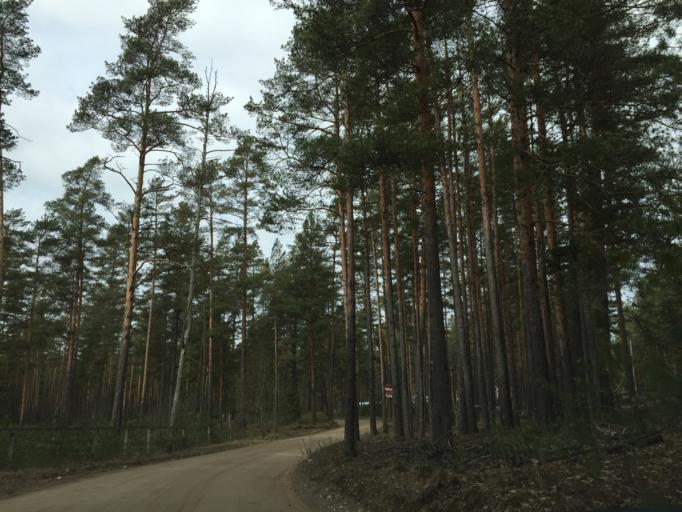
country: LV
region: Garkalne
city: Garkalne
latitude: 57.0690
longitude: 24.4641
